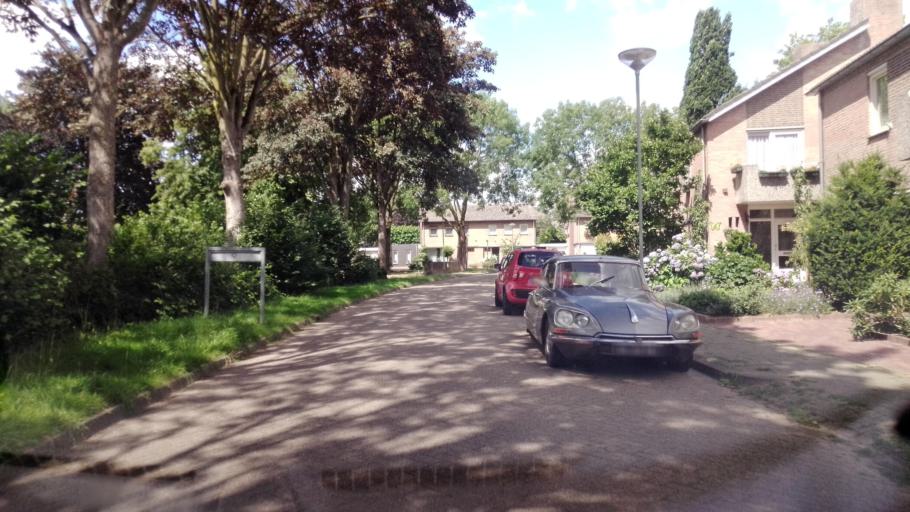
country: NL
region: Limburg
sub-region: Gemeente Venlo
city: Tegelen
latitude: 51.3271
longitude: 6.0953
